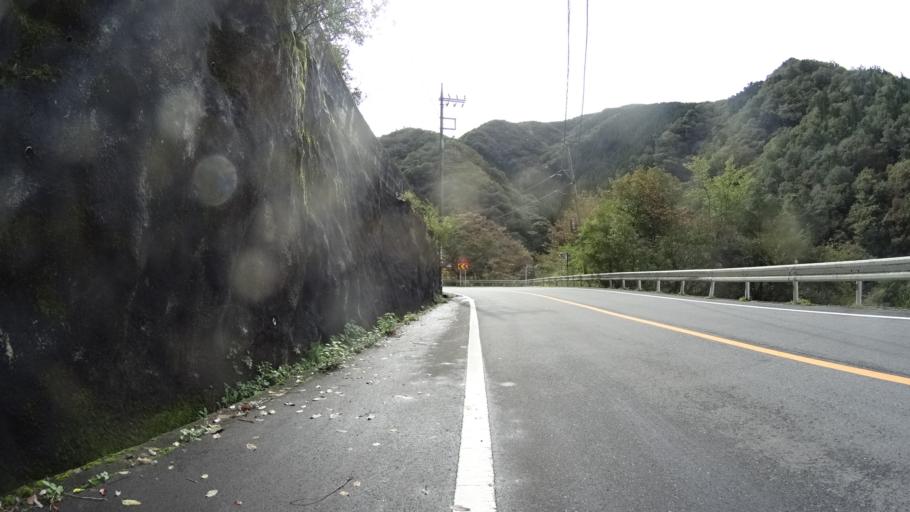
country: JP
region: Yamanashi
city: Otsuki
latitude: 35.7867
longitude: 138.9656
